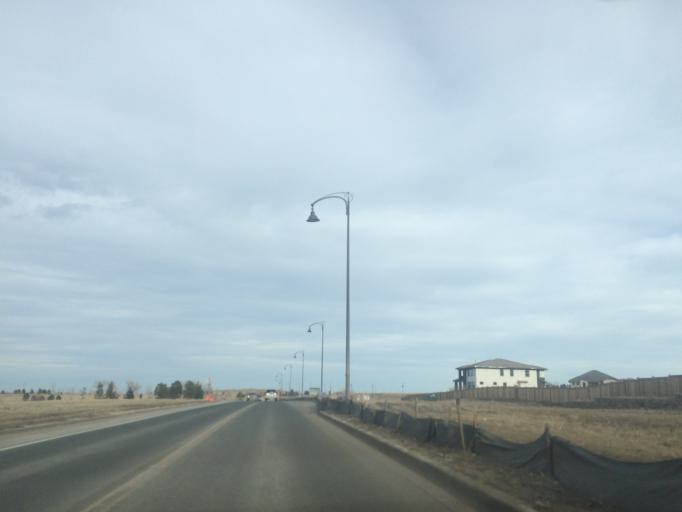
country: US
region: Colorado
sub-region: Boulder County
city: Lafayette
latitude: 39.9787
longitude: -105.0316
